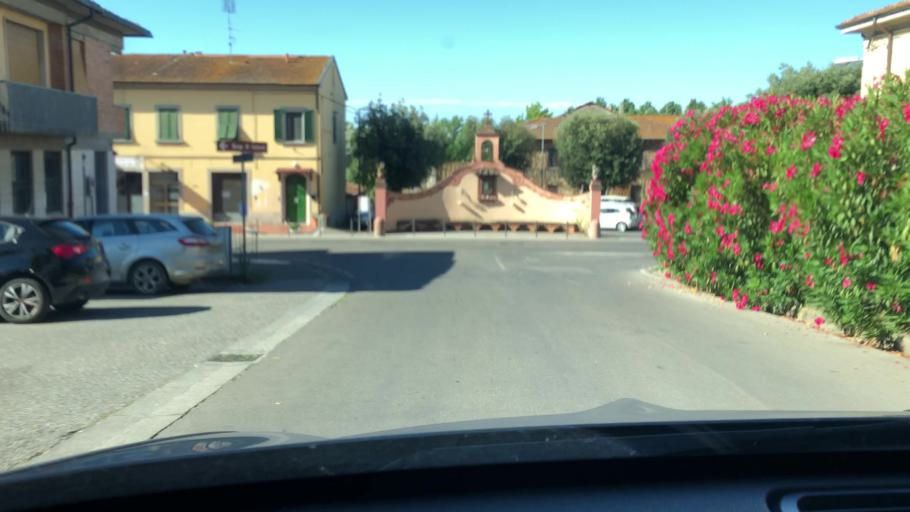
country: IT
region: Tuscany
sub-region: Province of Pisa
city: Forcoli
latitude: 43.6043
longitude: 10.7042
